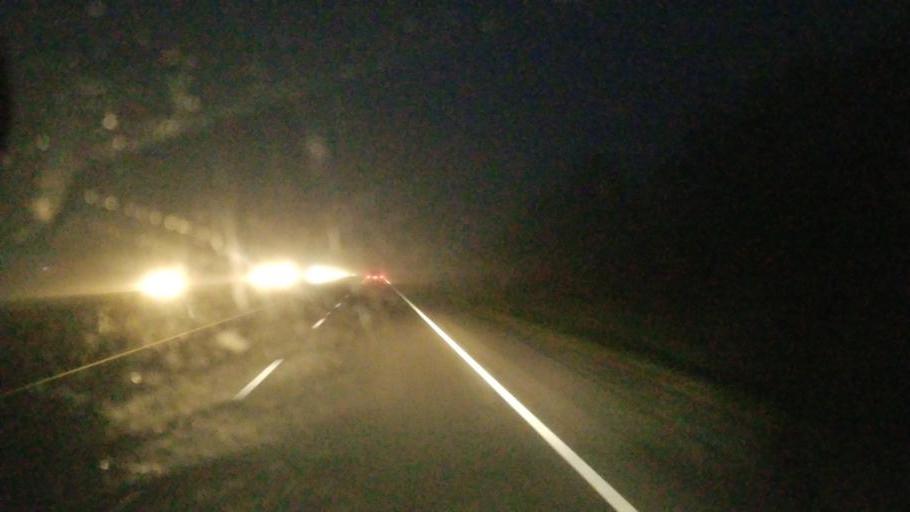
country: US
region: Ohio
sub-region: Ross County
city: Kingston
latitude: 39.4587
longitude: -82.9708
